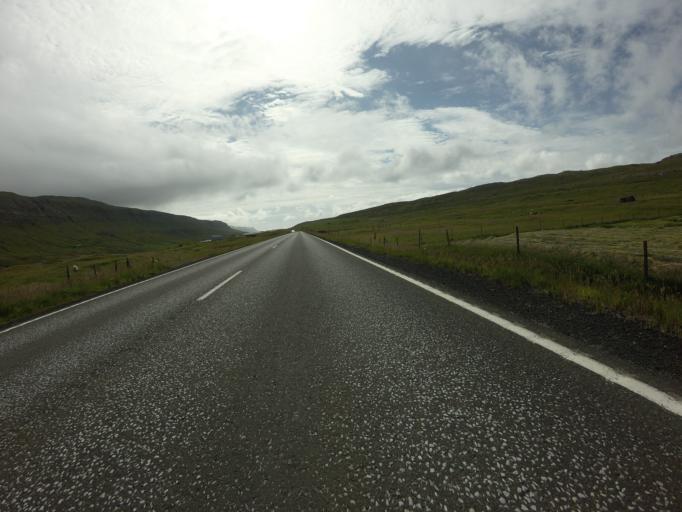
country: FO
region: Sandoy
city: Sandur
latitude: 61.8617
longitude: -6.8361
